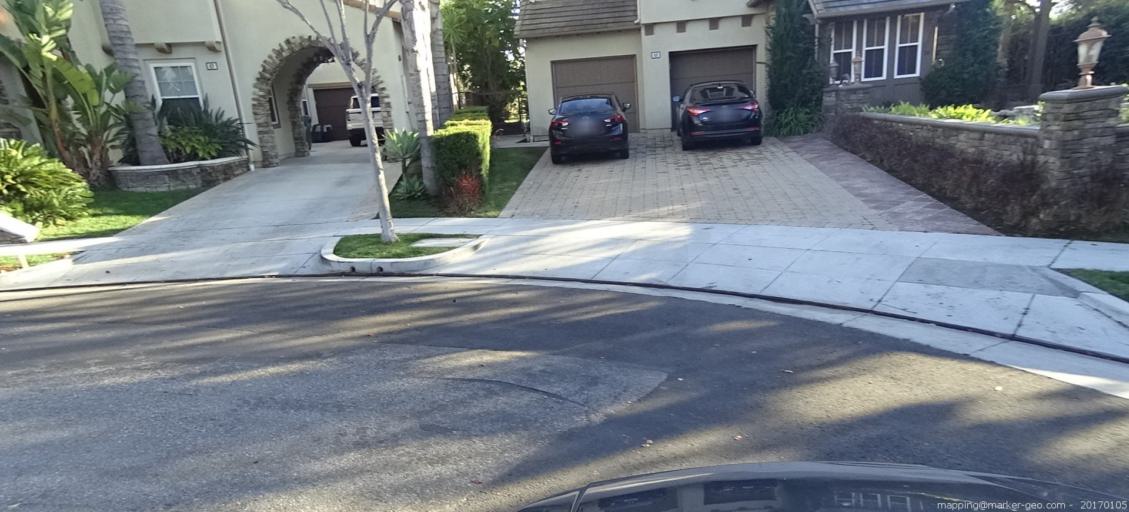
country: US
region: California
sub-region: Orange County
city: Ladera Ranch
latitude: 33.5460
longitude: -117.6414
